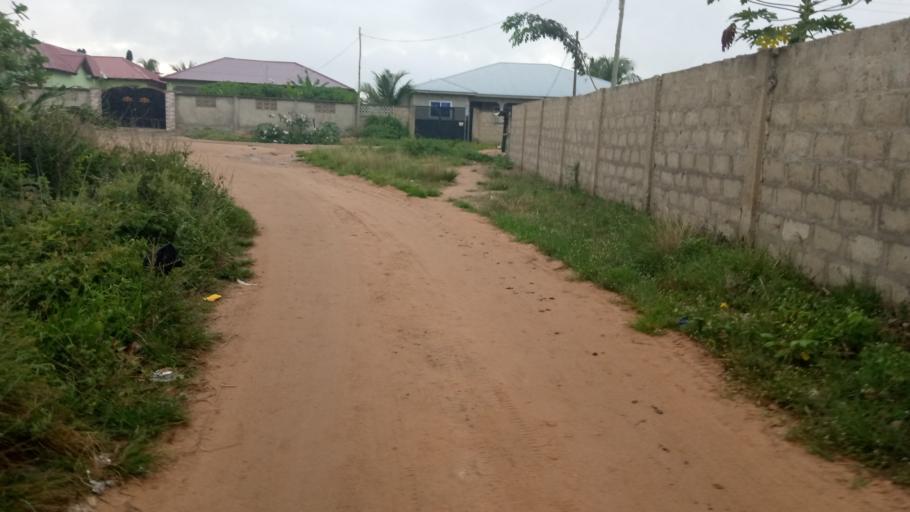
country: GH
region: Central
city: Kasoa
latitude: 5.4988
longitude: -0.4087
